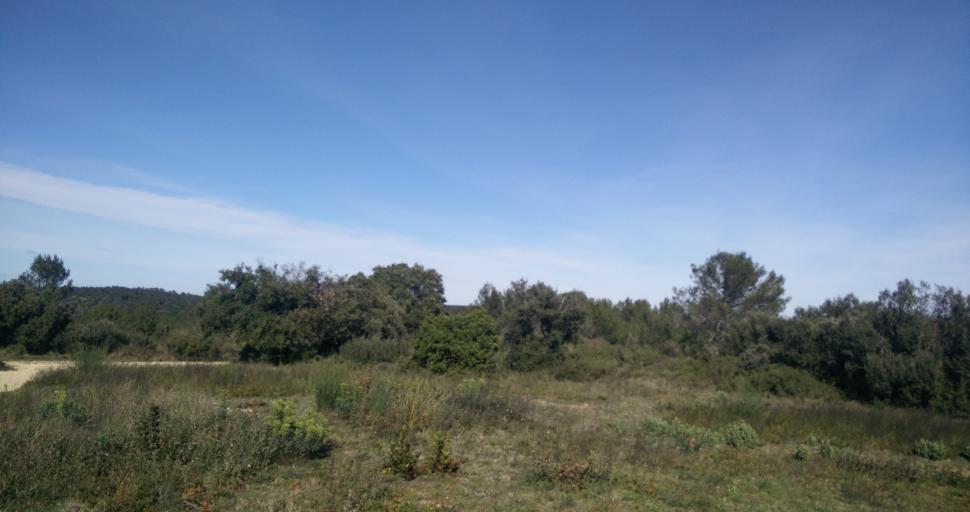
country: FR
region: Languedoc-Roussillon
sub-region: Departement du Gard
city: Calvisson
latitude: 43.8249
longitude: 4.1688
